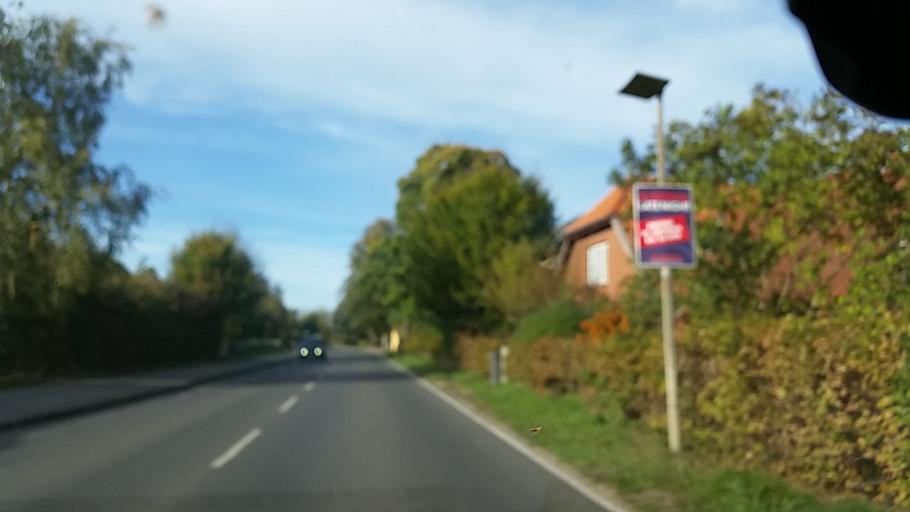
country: DE
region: Schleswig-Holstein
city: Jersbek
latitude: 53.7403
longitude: 10.2225
